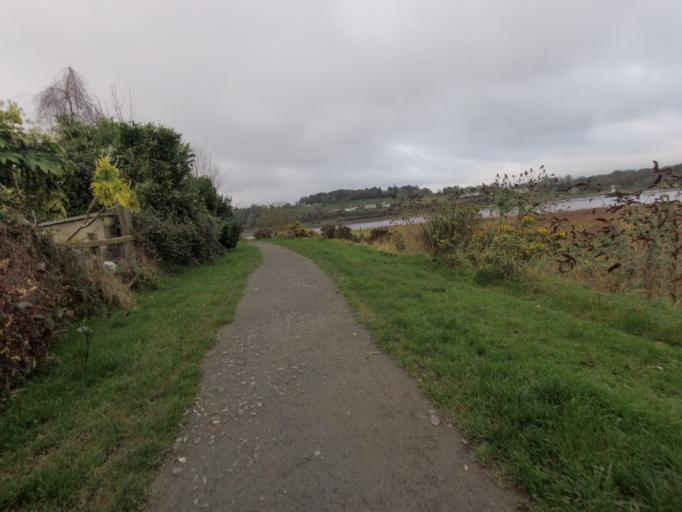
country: IE
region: Munster
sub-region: Waterford
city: Waterford
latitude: 52.2545
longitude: -7.0695
